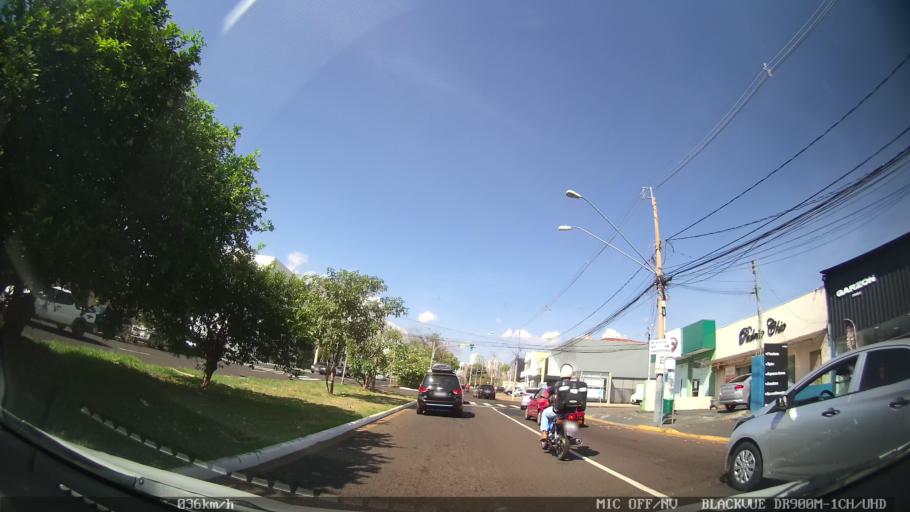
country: BR
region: Sao Paulo
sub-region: Ribeirao Preto
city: Ribeirao Preto
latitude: -21.2082
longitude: -47.8139
